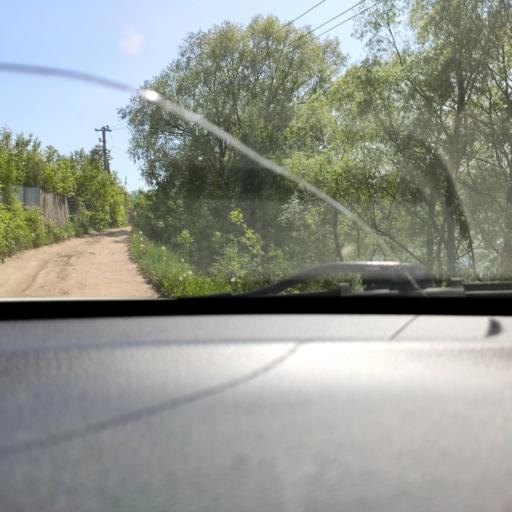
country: RU
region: Tatarstan
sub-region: Gorod Kazan'
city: Kazan
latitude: 55.8625
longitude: 49.1977
